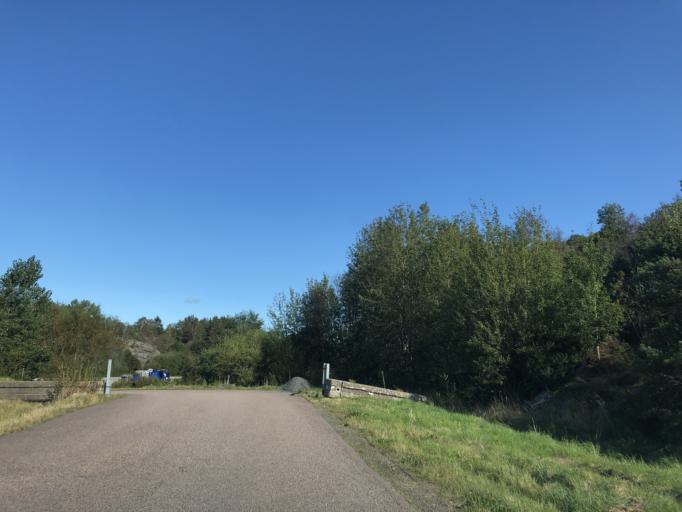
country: SE
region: Vaestra Goetaland
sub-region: Goteborg
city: Torslanda
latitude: 57.7164
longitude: 11.8088
